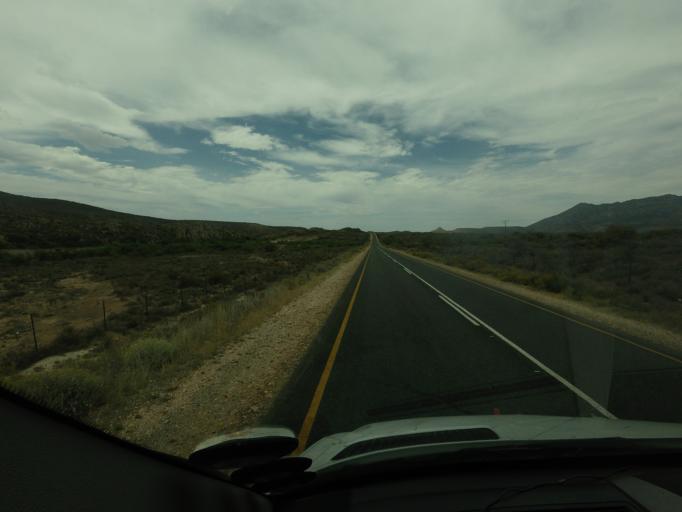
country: ZA
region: Western Cape
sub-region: Overberg District Municipality
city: Swellendam
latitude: -33.8522
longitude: 20.8184
